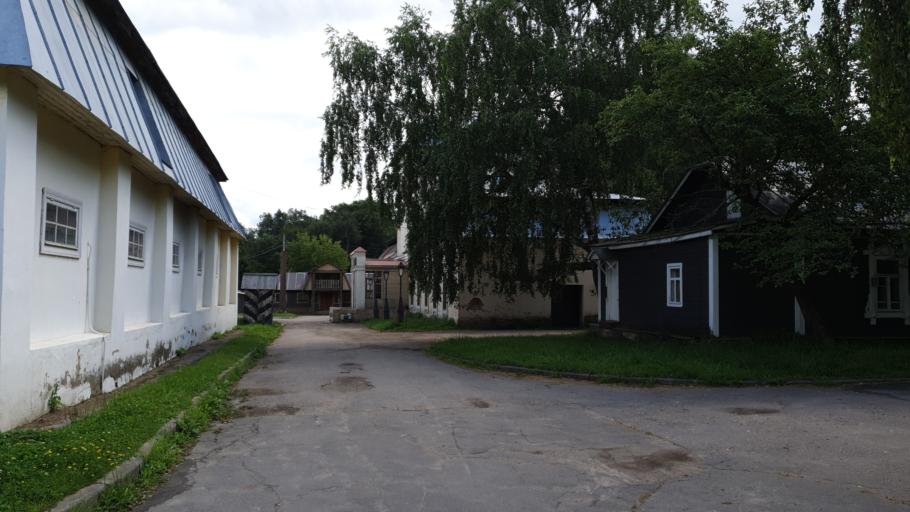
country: RU
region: Moskovskaya
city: Gorki-Leninskiye
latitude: 55.5066
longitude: 37.7701
